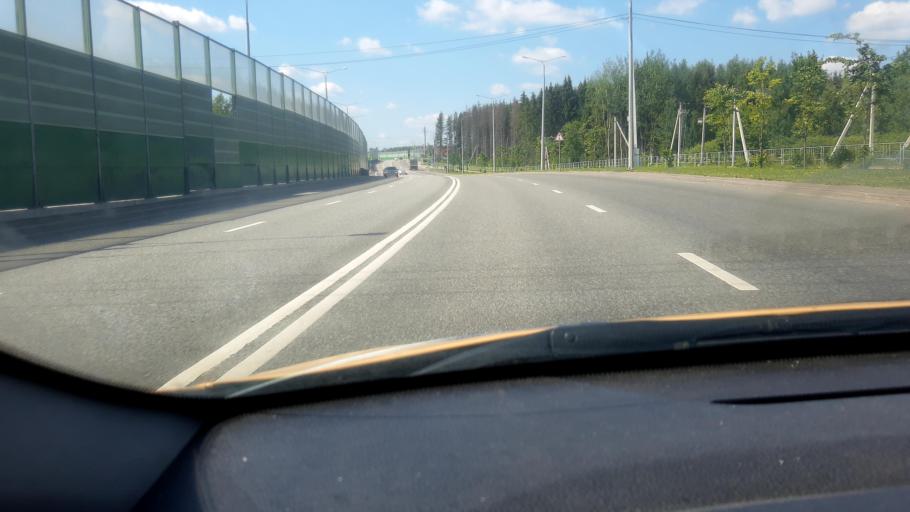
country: RU
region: Moskovskaya
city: Annino
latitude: 55.5269
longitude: 37.2374
